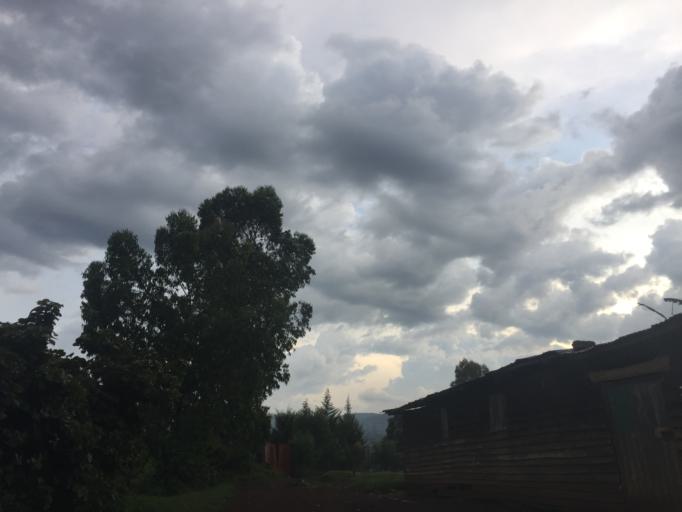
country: CD
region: South Kivu
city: Kabare
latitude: -2.4011
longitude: 28.8060
